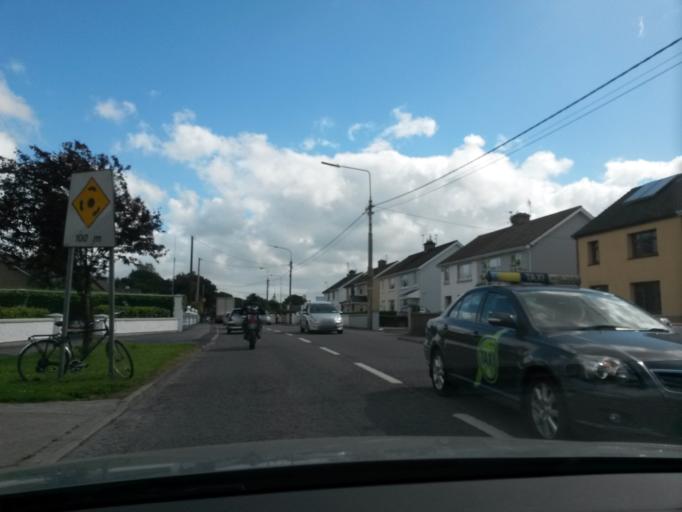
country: IE
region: Munster
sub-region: An Clar
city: Ennis
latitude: 52.8504
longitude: -8.9729
